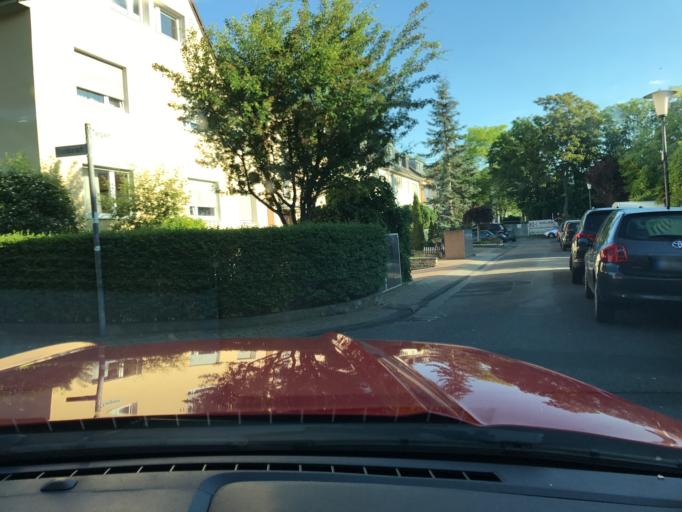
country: DE
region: North Rhine-Westphalia
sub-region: Regierungsbezirk Koln
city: Nippes
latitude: 50.9690
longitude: 6.9559
